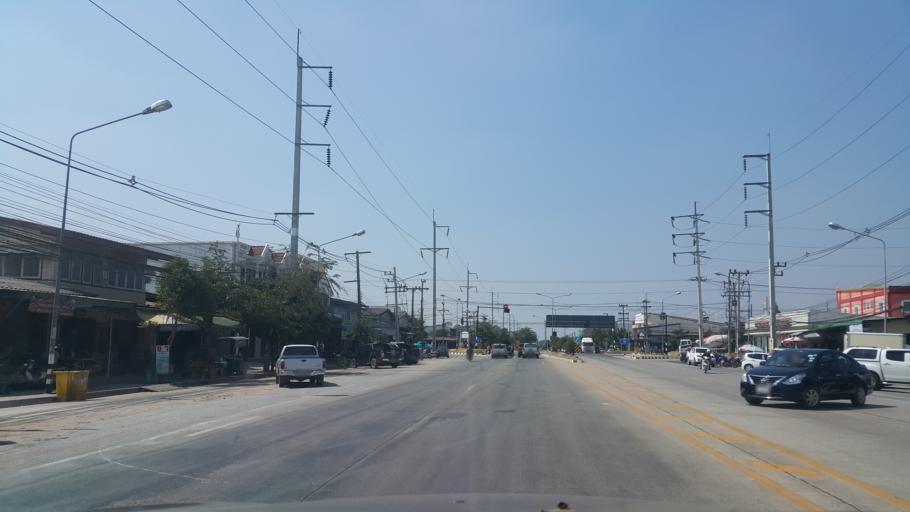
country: TH
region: Nakhon Ratchasima
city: Sida
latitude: 15.5471
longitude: 102.5492
